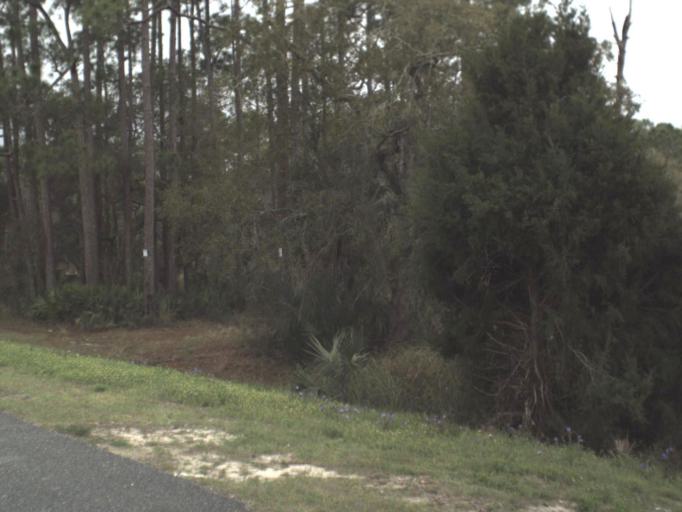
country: US
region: Florida
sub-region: Franklin County
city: Eastpoint
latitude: 29.8193
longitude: -84.8498
